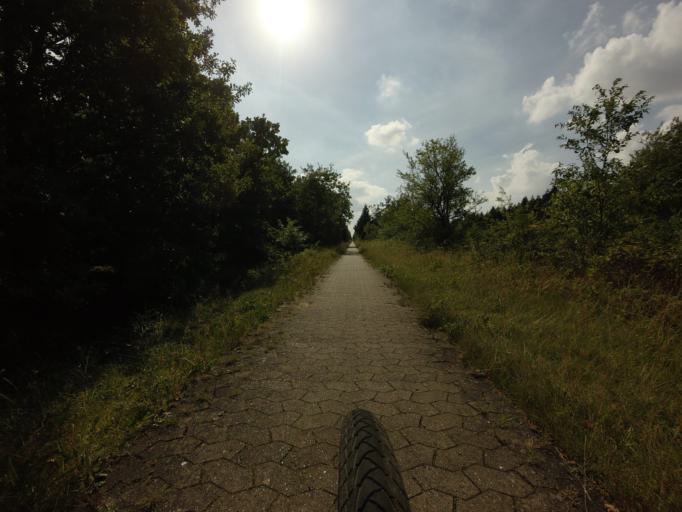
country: DK
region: Central Jutland
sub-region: Viborg Kommune
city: Karup
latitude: 56.2742
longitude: 9.1190
